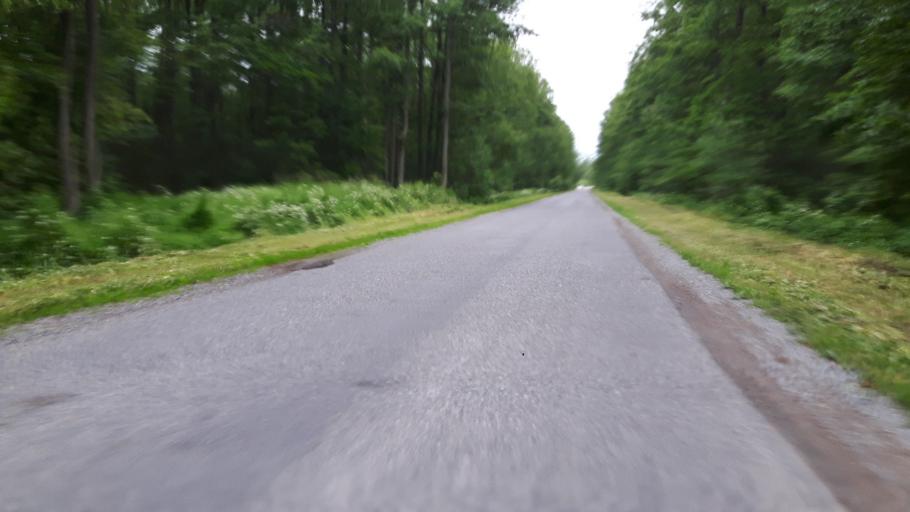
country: LV
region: Liepaja
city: Vec-Liepaja
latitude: 56.5792
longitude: 21.0261
